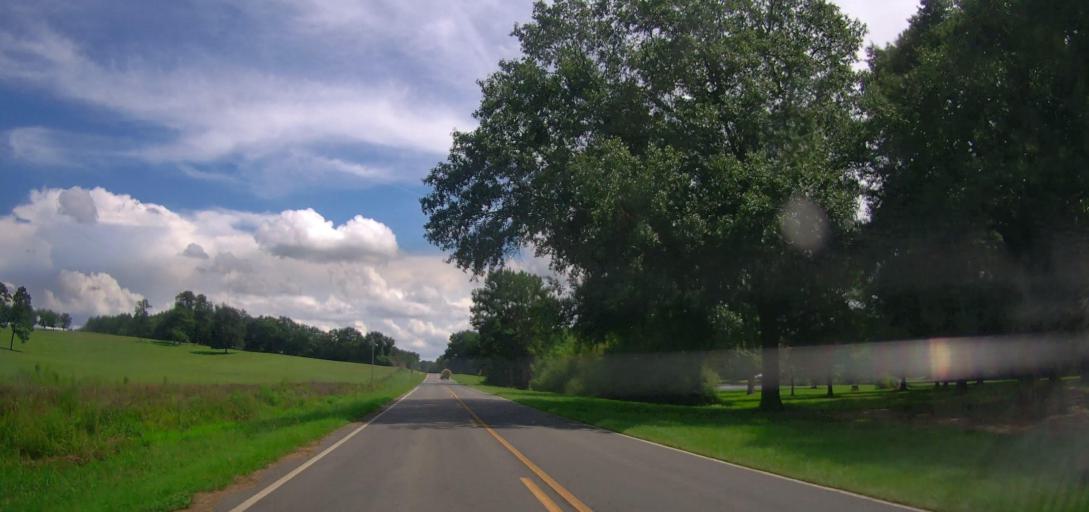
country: US
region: Georgia
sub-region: Taylor County
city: Butler
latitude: 32.5413
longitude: -84.2226
